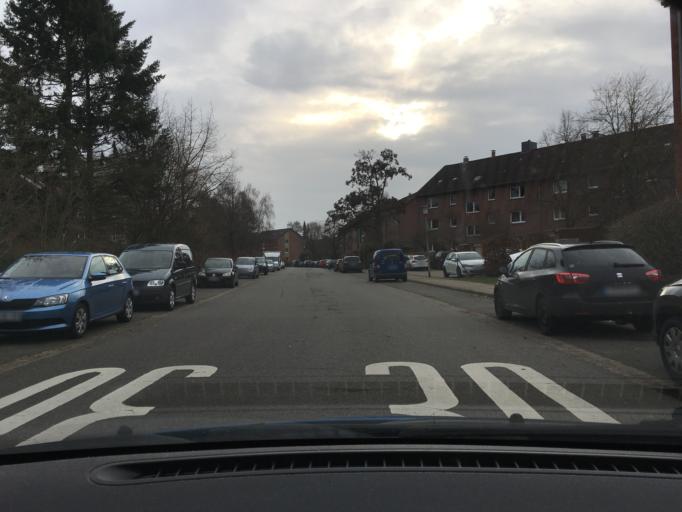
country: DE
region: Lower Saxony
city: Lueneburg
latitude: 53.2600
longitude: 10.3924
